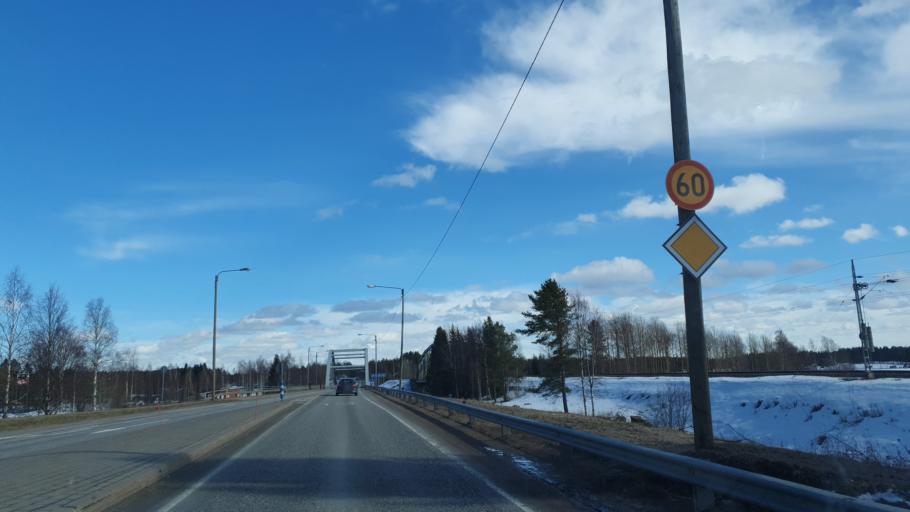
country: FI
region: Kainuu
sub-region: Kajaani
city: Paltamo
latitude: 64.4030
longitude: 27.8396
